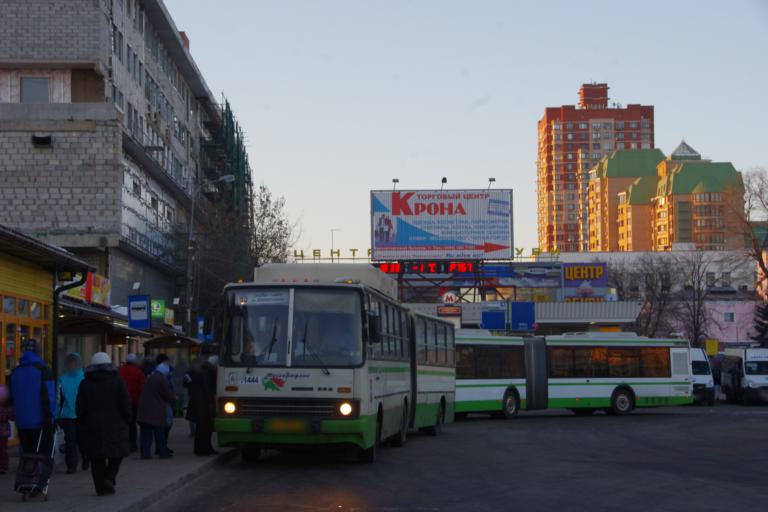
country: RU
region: Moskovskaya
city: Levoberezhnyy
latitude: 55.8399
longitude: 37.4867
